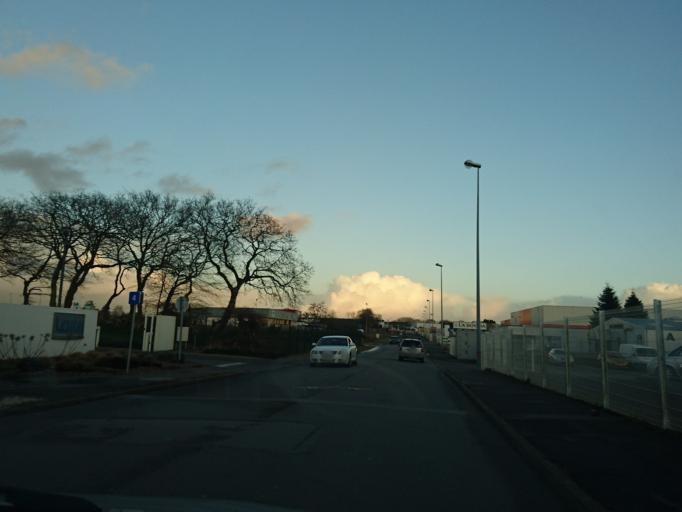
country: FR
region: Brittany
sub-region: Departement du Finistere
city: Gouesnou
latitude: 48.4315
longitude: -4.4510
